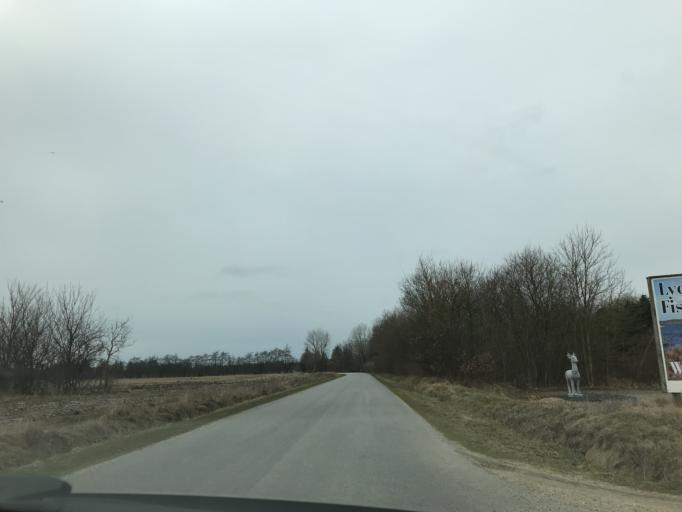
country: DK
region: South Denmark
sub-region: Varde Kommune
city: Oksbol
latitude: 55.8044
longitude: 8.3459
